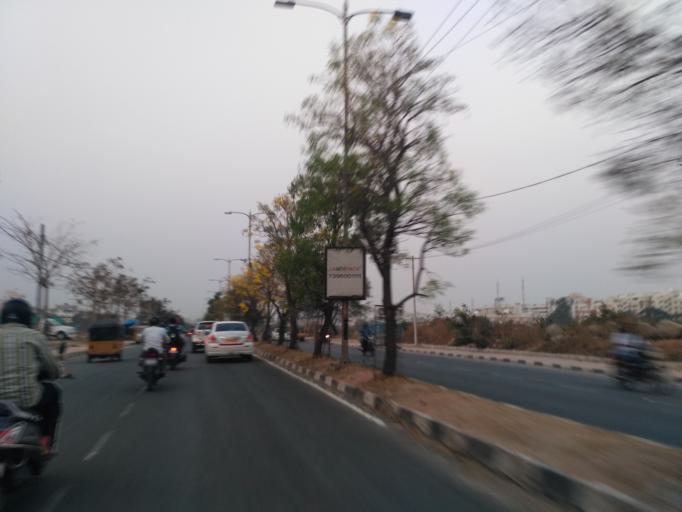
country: IN
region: Telangana
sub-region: Rangareddi
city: Kukatpalli
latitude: 17.4447
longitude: 78.3941
